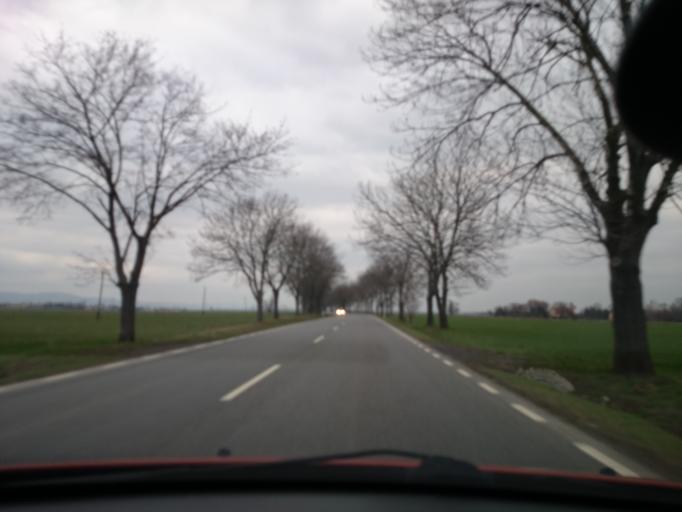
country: PL
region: Opole Voivodeship
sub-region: Powiat nyski
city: Otmuchow
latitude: 50.4478
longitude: 17.0999
